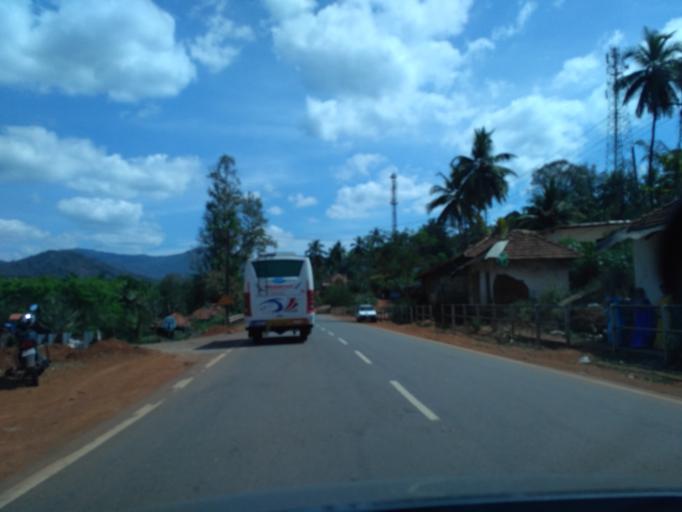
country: IN
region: Karnataka
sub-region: Dakshina Kannada
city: Sulya
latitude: 12.4999
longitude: 75.5421
